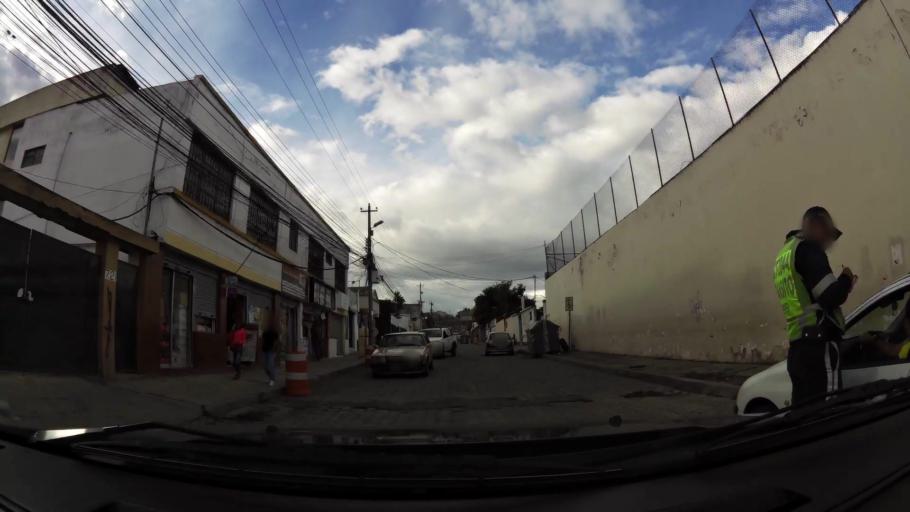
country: EC
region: Pichincha
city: Quito
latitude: -0.1520
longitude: -78.4725
